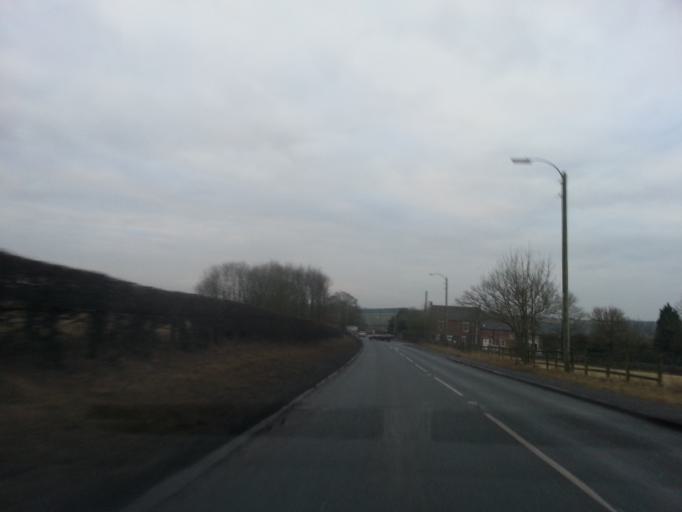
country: GB
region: England
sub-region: County Durham
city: High Etherley
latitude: 54.6423
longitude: -1.7448
